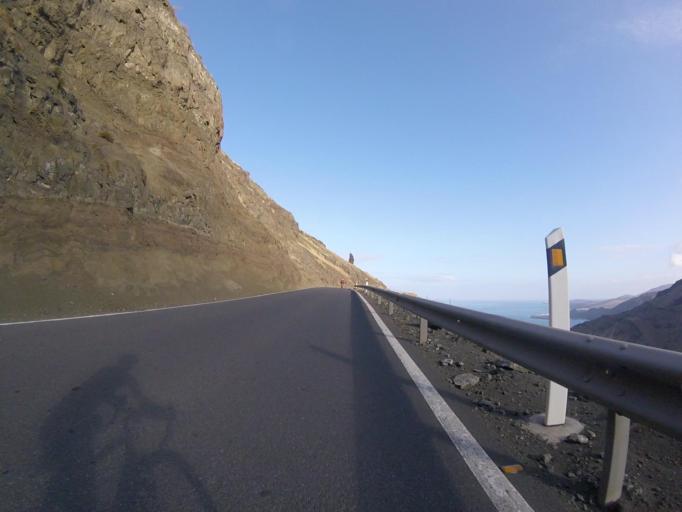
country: ES
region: Canary Islands
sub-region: Provincia de Las Palmas
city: Agaete
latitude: 28.0728
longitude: -15.7137
